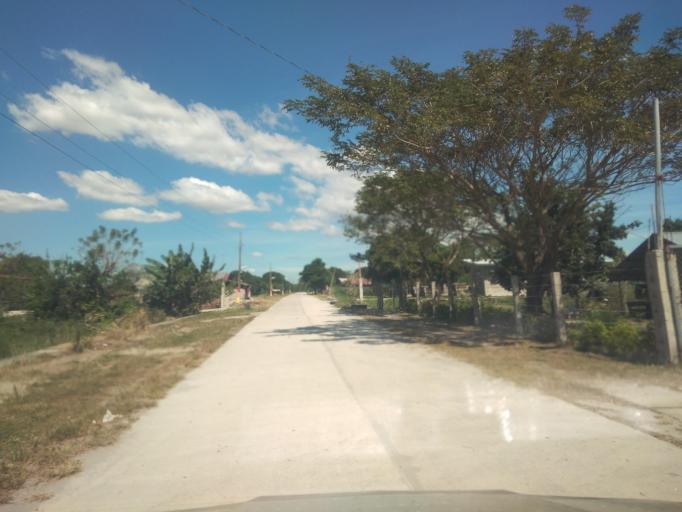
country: PH
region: Central Luzon
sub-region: Province of Pampanga
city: San Basilio
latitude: 15.0290
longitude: 120.6055
